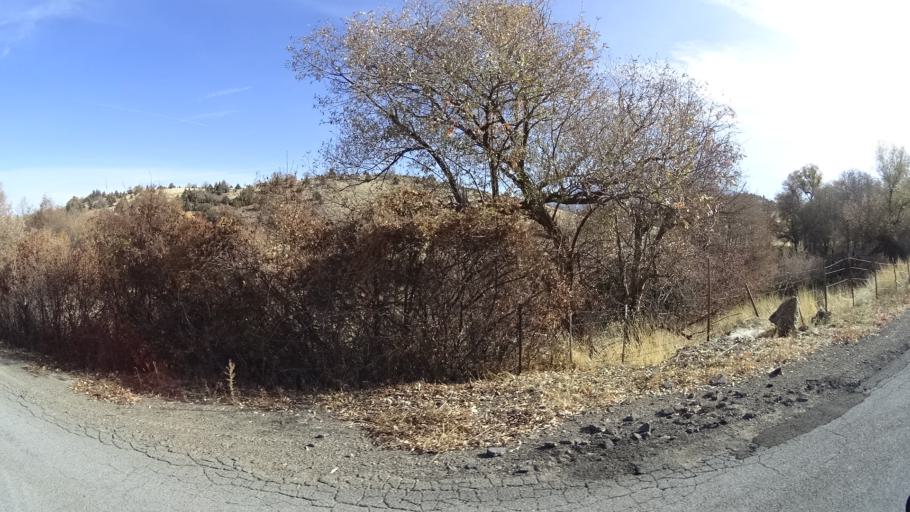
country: US
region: California
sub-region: Siskiyou County
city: Weed
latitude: 41.4756
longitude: -122.4407
